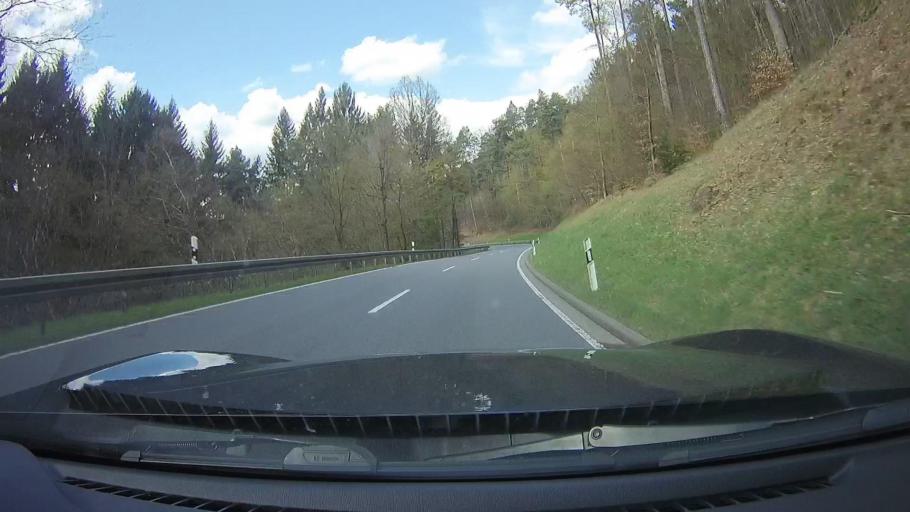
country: DE
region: Baden-Wuerttemberg
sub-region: Karlsruhe Region
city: Mudau
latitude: 49.5810
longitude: 9.2136
